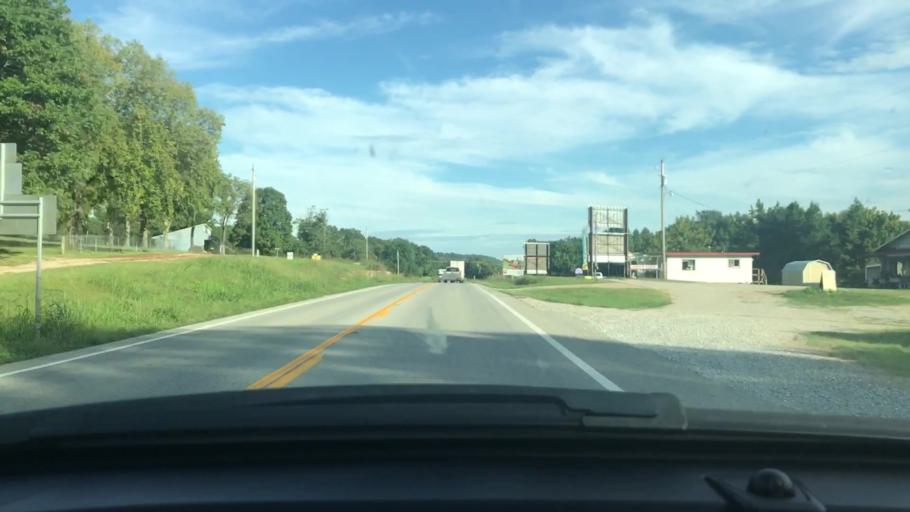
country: US
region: Arkansas
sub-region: Sharp County
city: Cherokee Village
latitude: 36.3012
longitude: -91.4431
